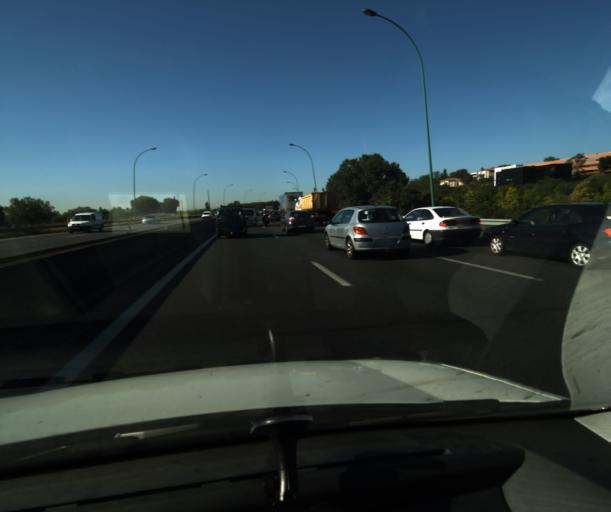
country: FR
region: Midi-Pyrenees
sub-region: Departement de la Haute-Garonne
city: Balma
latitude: 43.5788
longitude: 1.4982
